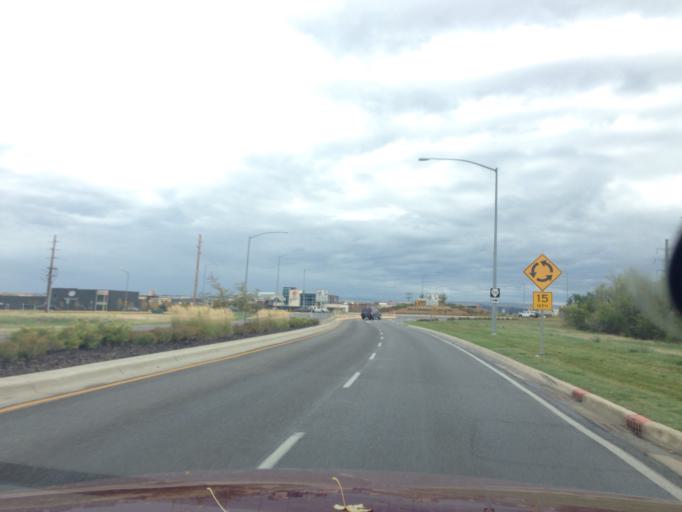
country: US
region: Montana
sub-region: Yellowstone County
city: Billings
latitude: 45.7566
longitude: -108.6177
